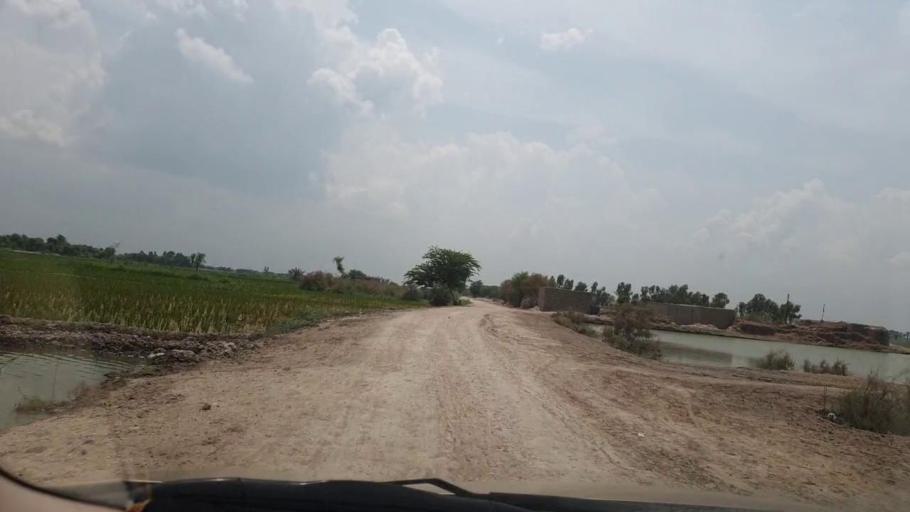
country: PK
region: Sindh
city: Larkana
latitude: 27.6208
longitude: 68.1555
